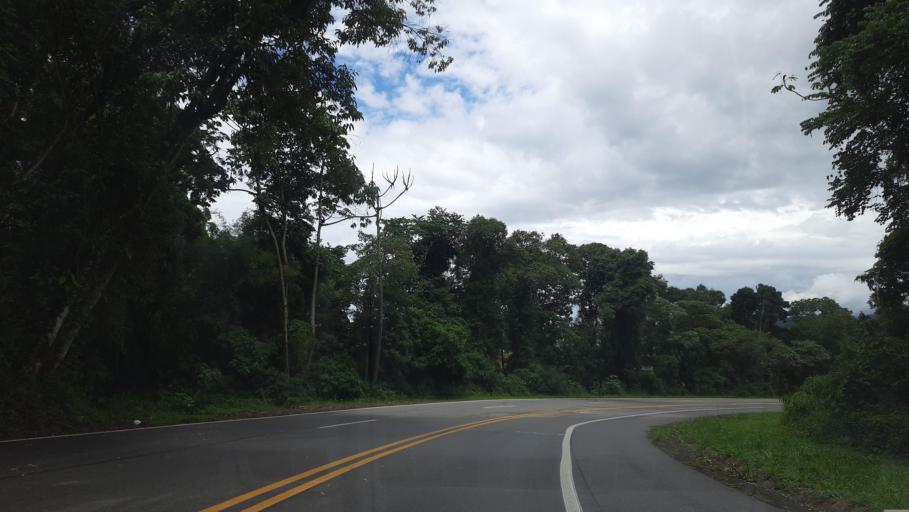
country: BR
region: Minas Gerais
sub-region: Pocos De Caldas
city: Pocos de Caldas
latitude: -21.8423
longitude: -46.6860
